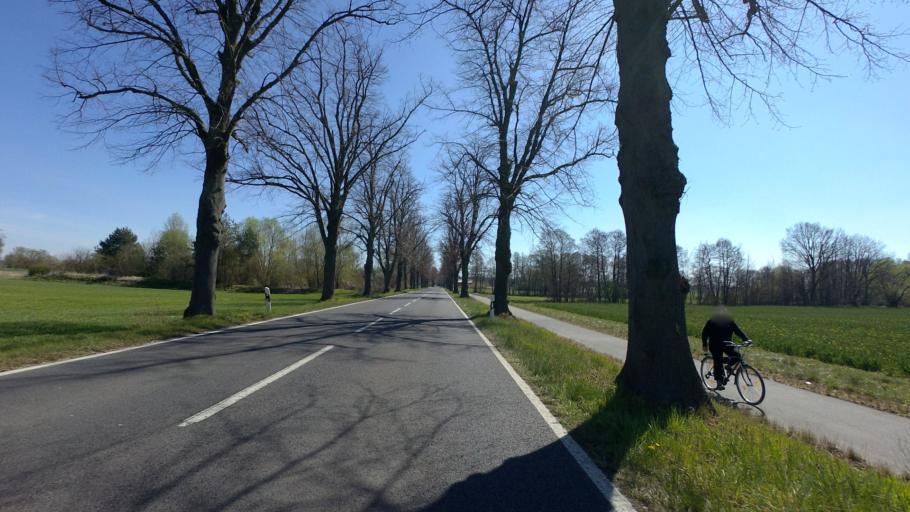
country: DE
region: Brandenburg
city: Schulzendorf
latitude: 52.3468
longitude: 13.5430
